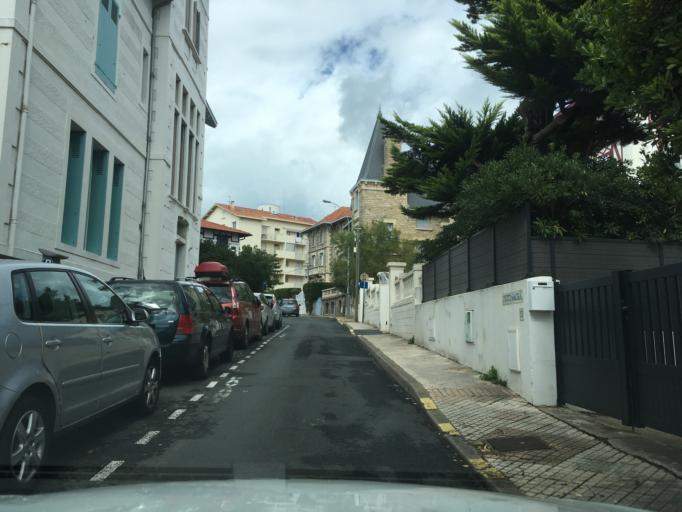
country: FR
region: Aquitaine
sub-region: Departement des Pyrenees-Atlantiques
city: Biarritz
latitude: 43.4864
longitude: -1.5536
